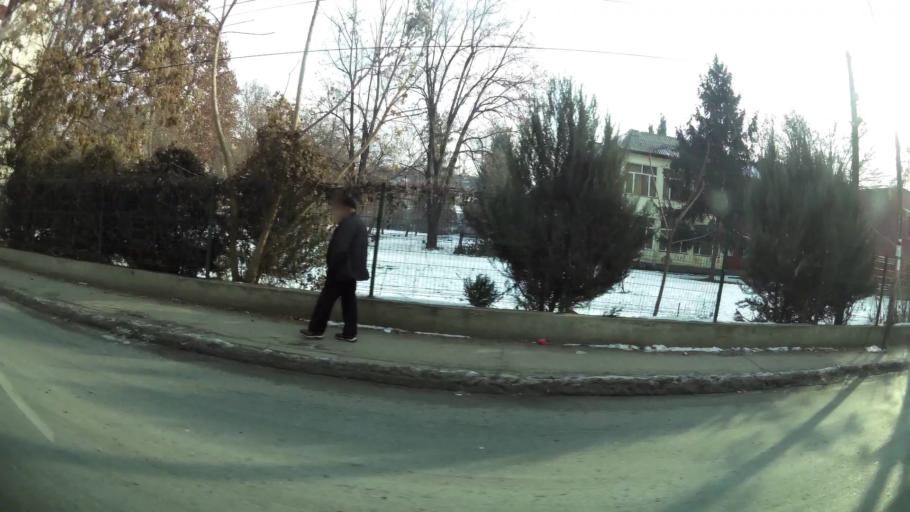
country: MK
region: Cair
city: Cair
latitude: 42.0195
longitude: 21.4325
